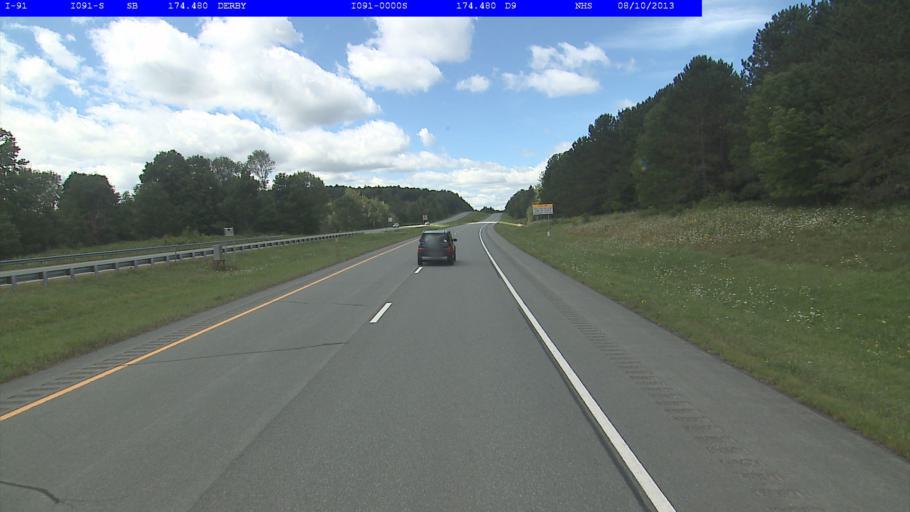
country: US
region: Vermont
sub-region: Orleans County
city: Newport
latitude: 44.9751
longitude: -72.1258
